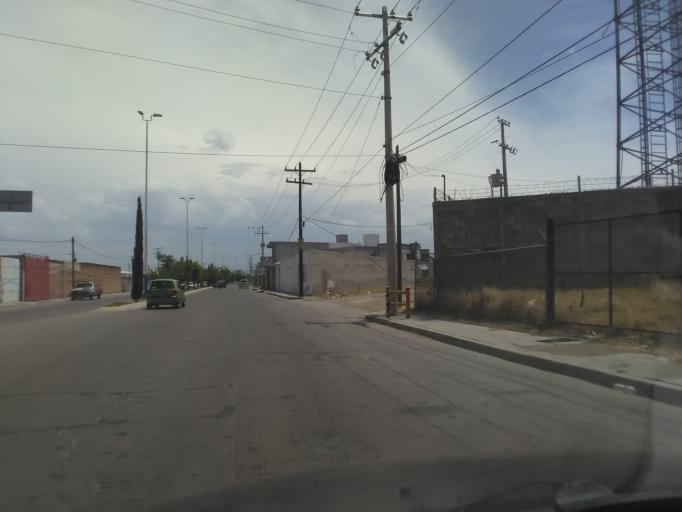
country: MX
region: Durango
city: Victoria de Durango
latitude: 24.0298
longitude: -104.6137
